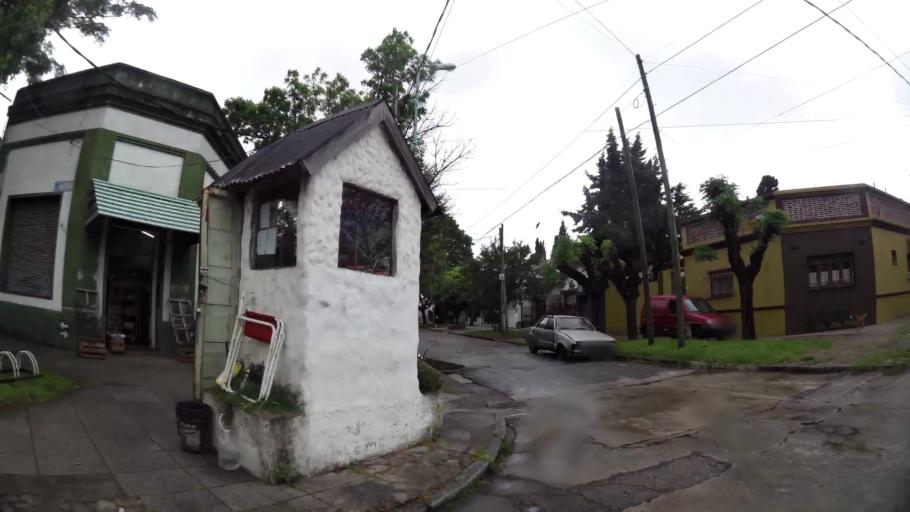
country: AR
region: Buenos Aires
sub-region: Partido de Lomas de Zamora
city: Lomas de Zamora
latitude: -34.7400
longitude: -58.3844
